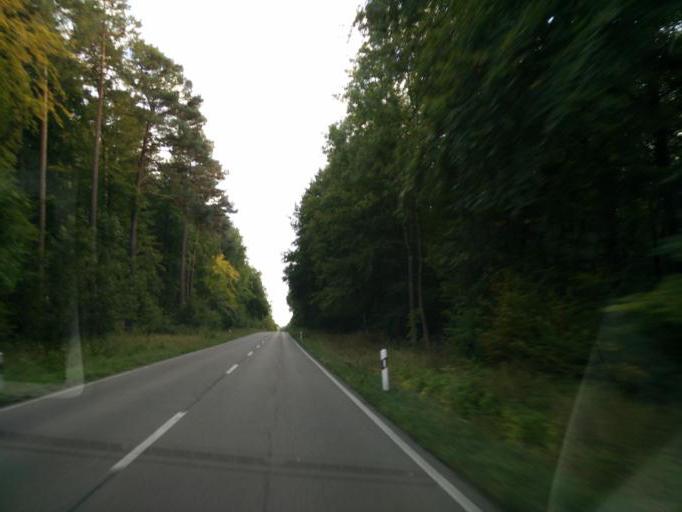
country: DE
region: Baden-Wuerttemberg
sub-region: Tuebingen Region
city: Dettenhausen
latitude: 48.5892
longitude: 9.1064
